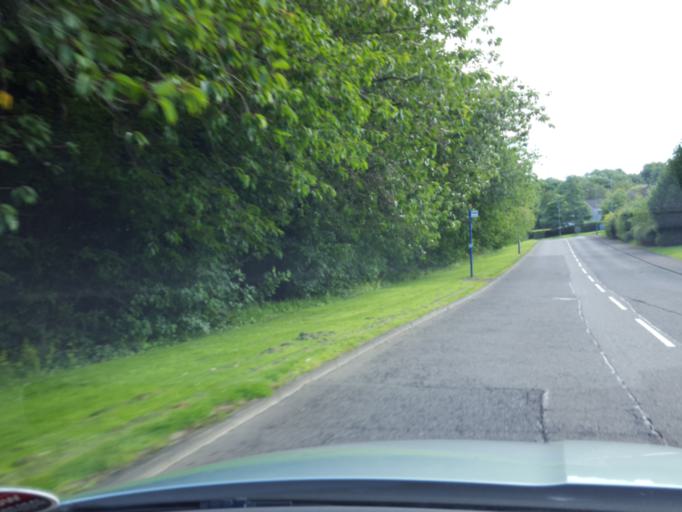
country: GB
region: Scotland
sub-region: Falkirk
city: Bo'ness
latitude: 56.0067
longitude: -3.6307
